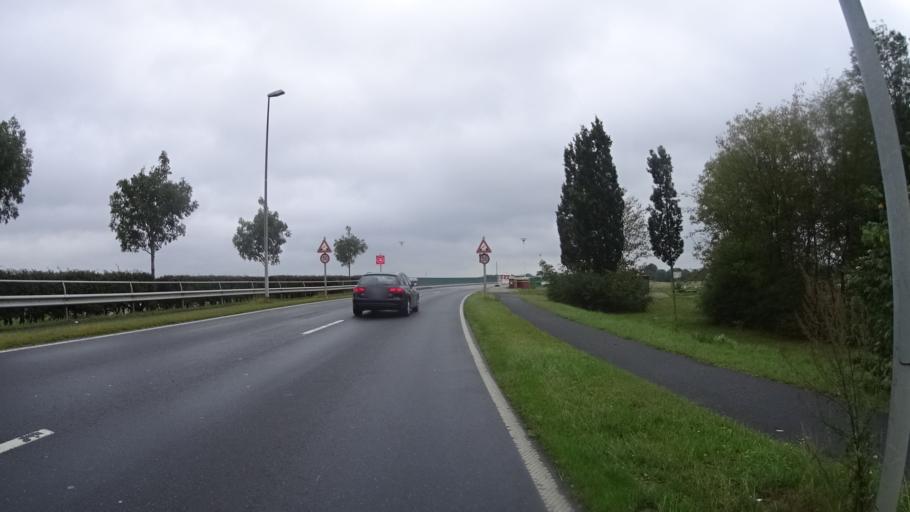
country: DE
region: Lower Saxony
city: Leer
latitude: 53.2185
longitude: 7.4221
